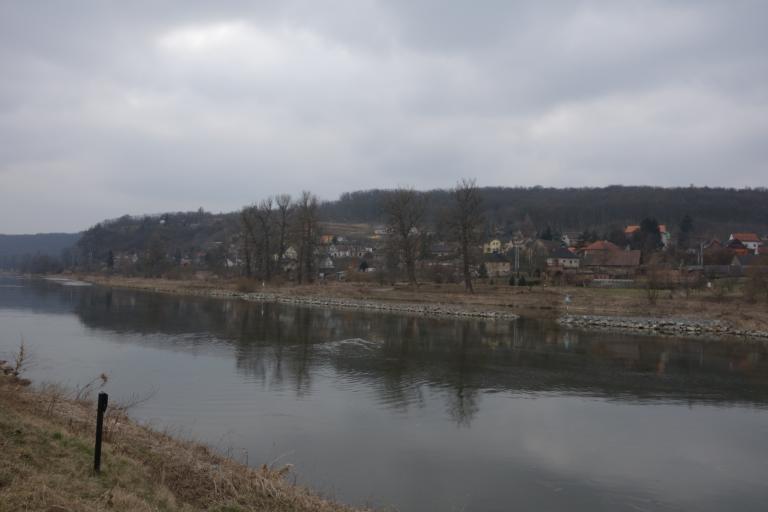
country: CZ
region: Central Bohemia
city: Libcice nad Vltavou
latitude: 50.2223
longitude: 14.3532
